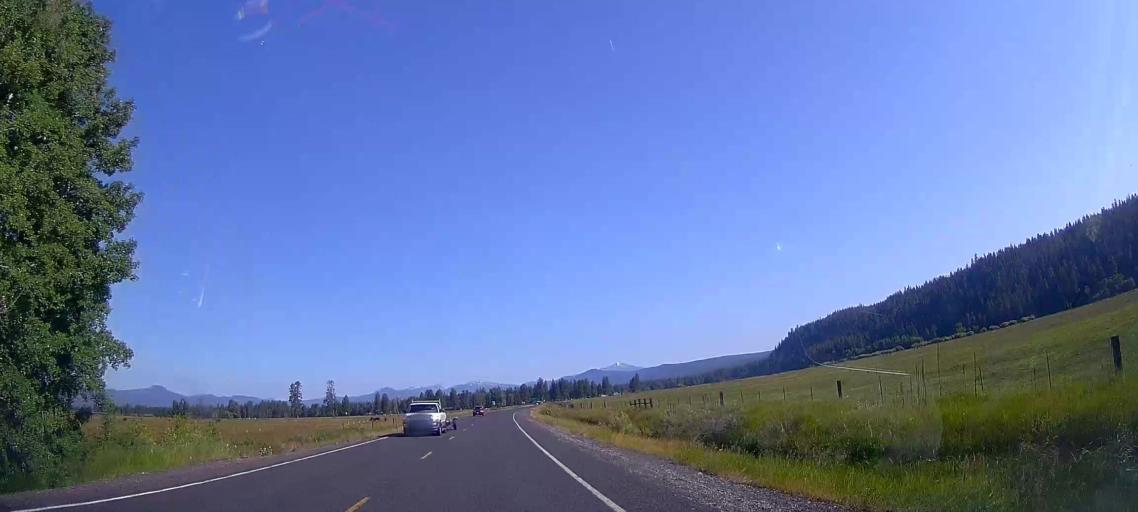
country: US
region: Oregon
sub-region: Klamath County
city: Klamath Falls
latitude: 42.6650
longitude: -121.9659
